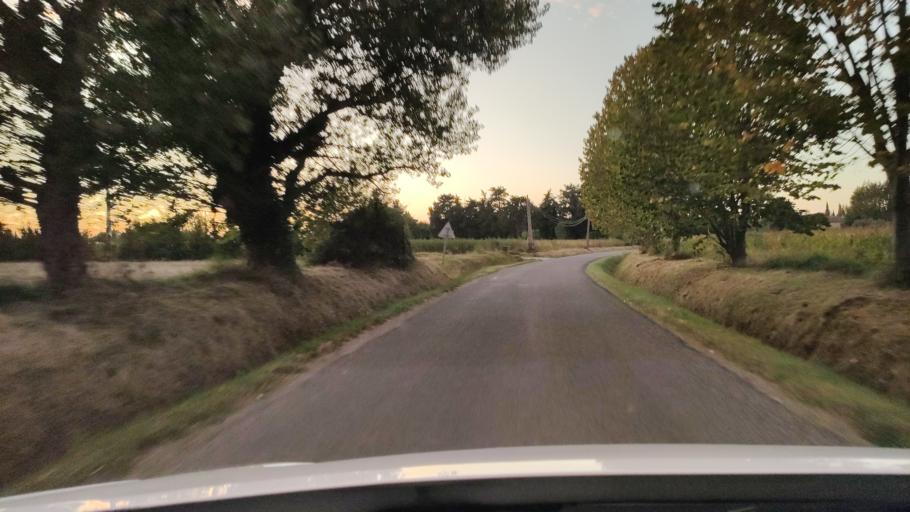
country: FR
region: Provence-Alpes-Cote d'Azur
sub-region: Departement du Vaucluse
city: Le Thor
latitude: 43.9359
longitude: 4.9880
